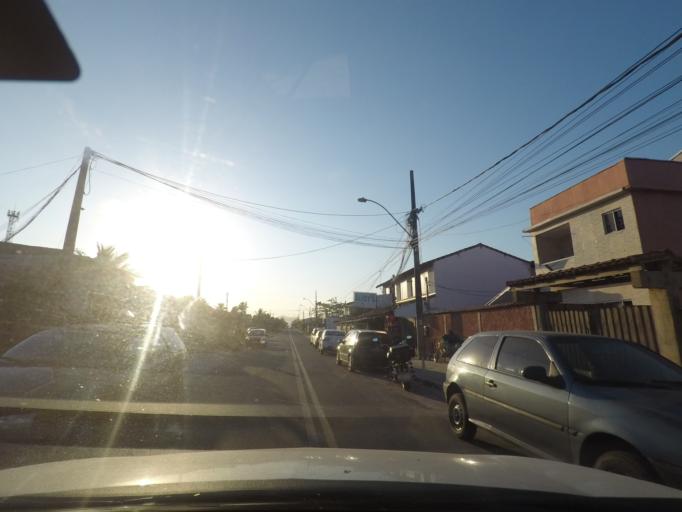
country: BR
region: Rio de Janeiro
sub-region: Marica
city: Marica
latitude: -22.9670
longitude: -42.9326
